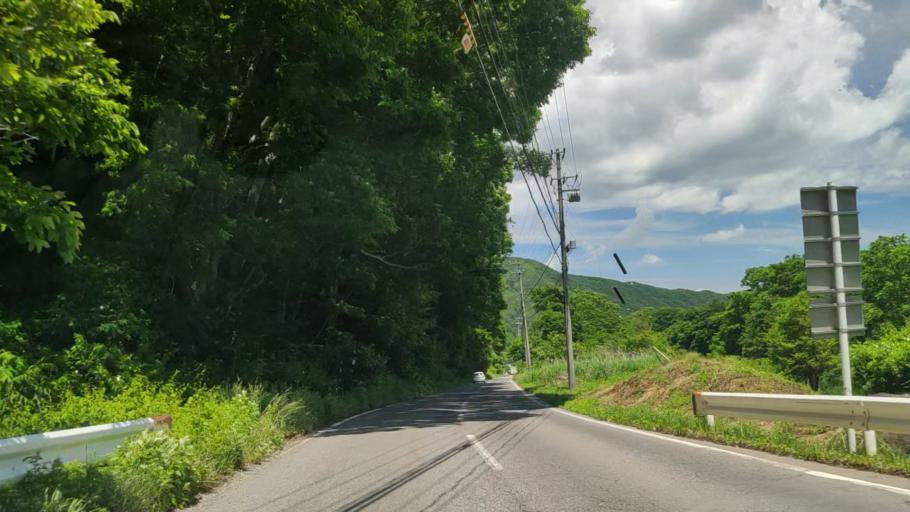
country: JP
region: Nagano
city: Kamimaruko
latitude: 36.1944
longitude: 138.2434
